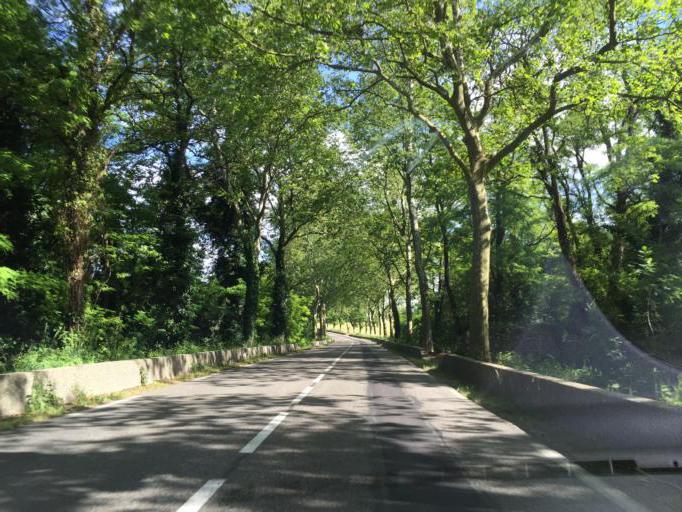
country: FR
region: Rhone-Alpes
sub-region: Departement de la Drome
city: Saulce-sur-Rhone
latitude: 44.6971
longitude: 4.7693
